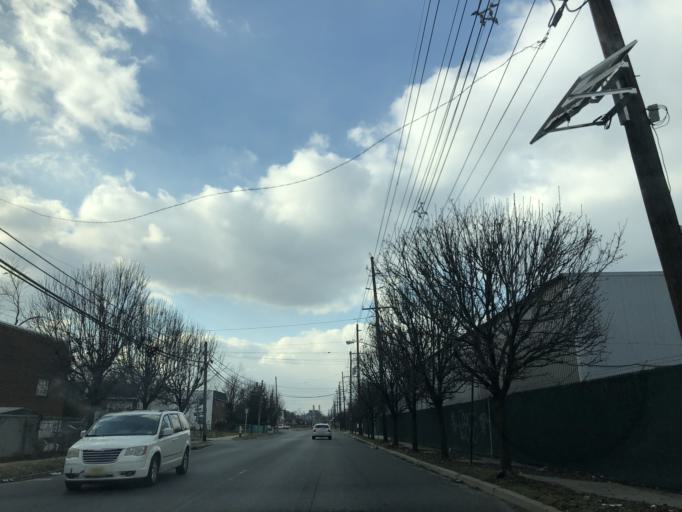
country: US
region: New Jersey
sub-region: Camden County
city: Wood-Lynne
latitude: 39.9139
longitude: -75.1044
